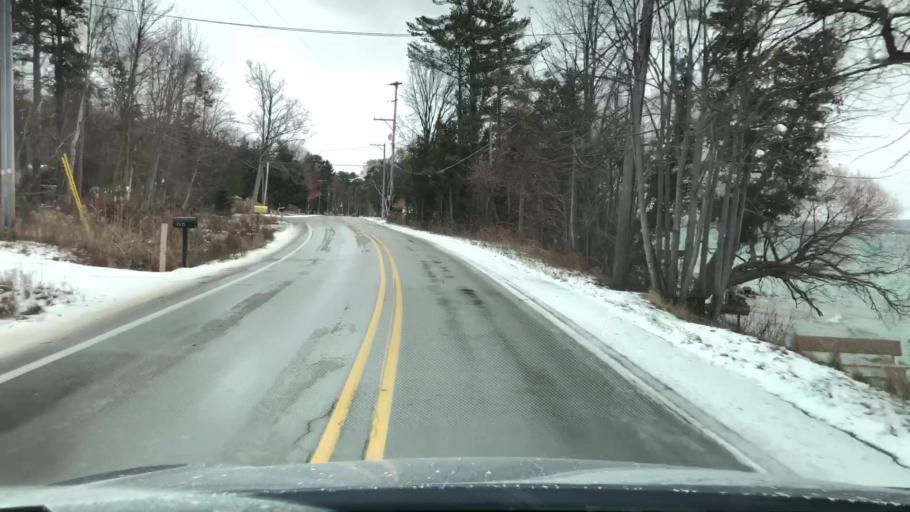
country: US
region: Michigan
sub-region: Grand Traverse County
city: Traverse City
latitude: 44.7967
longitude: -85.5851
